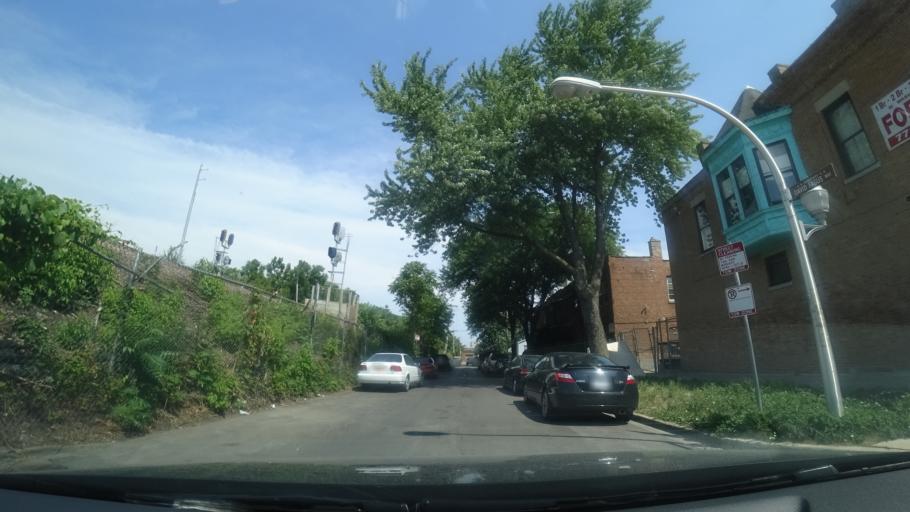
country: US
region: Illinois
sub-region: Cook County
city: Evanston
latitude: 42.0102
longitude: -87.6754
